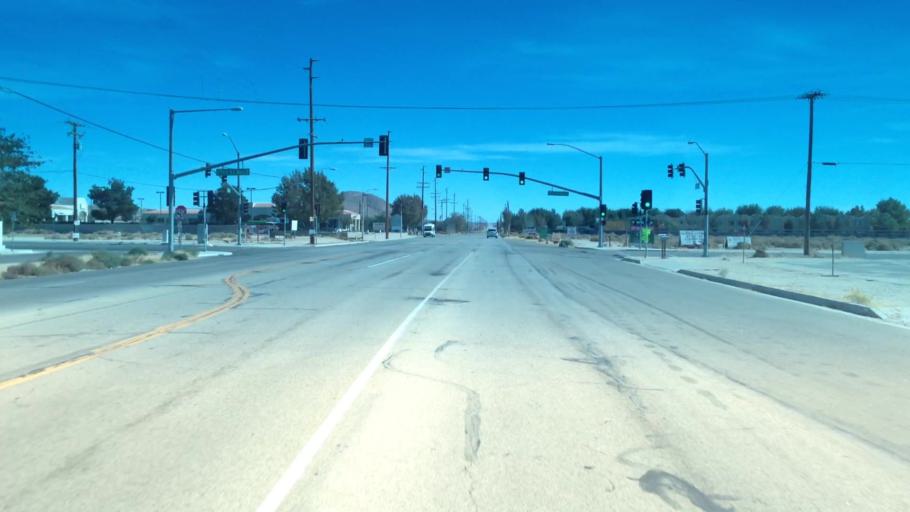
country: US
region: California
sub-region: Kern County
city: Rosamond
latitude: 34.8644
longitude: -118.1592
